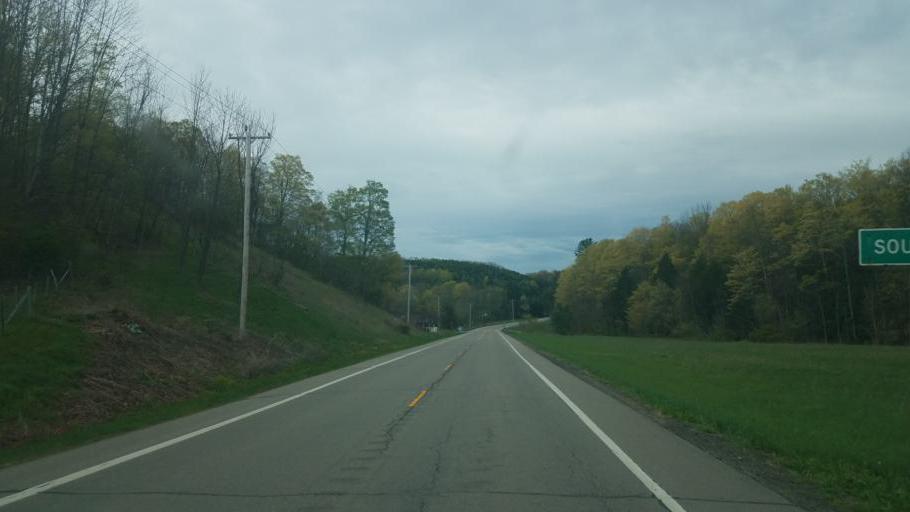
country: US
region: New York
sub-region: Steuben County
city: Canisteo
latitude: 42.1977
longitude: -77.5525
